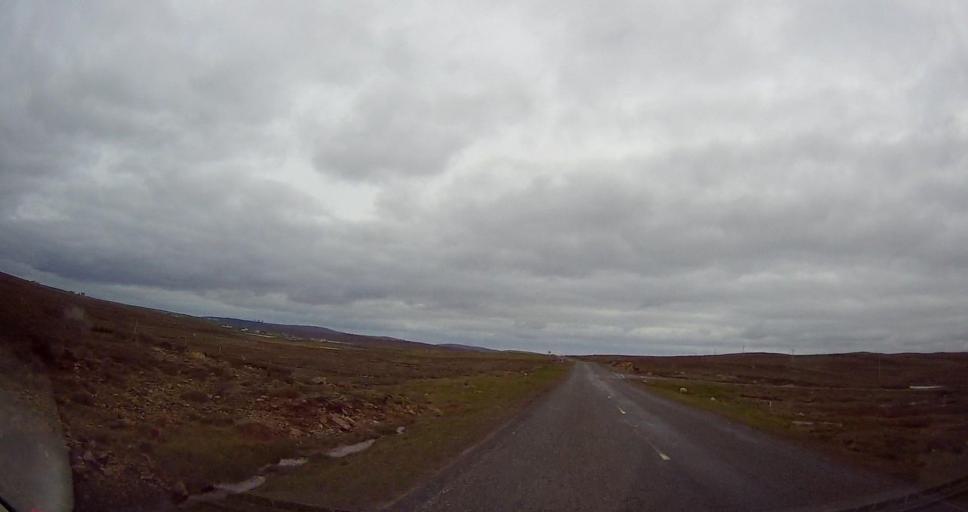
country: GB
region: Scotland
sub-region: Shetland Islands
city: Shetland
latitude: 60.7066
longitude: -0.9195
